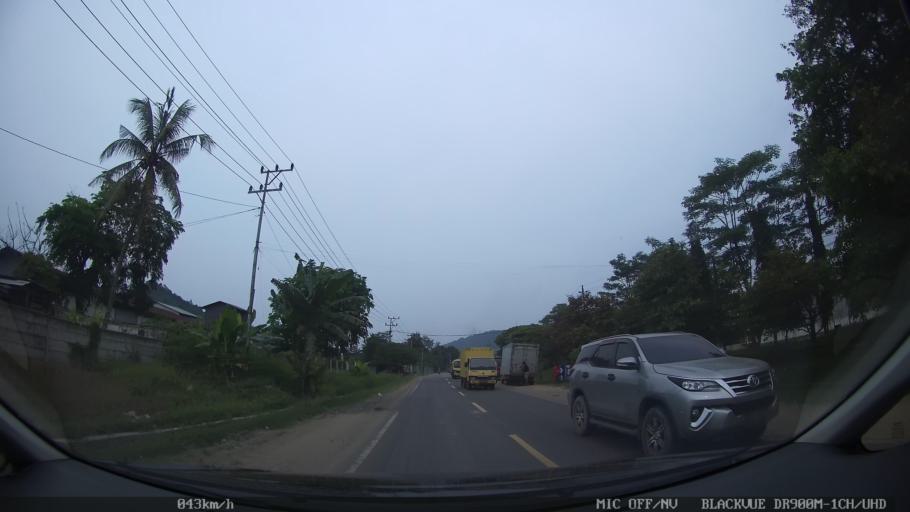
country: ID
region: Lampung
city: Panjang
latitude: -5.4186
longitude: 105.3408
